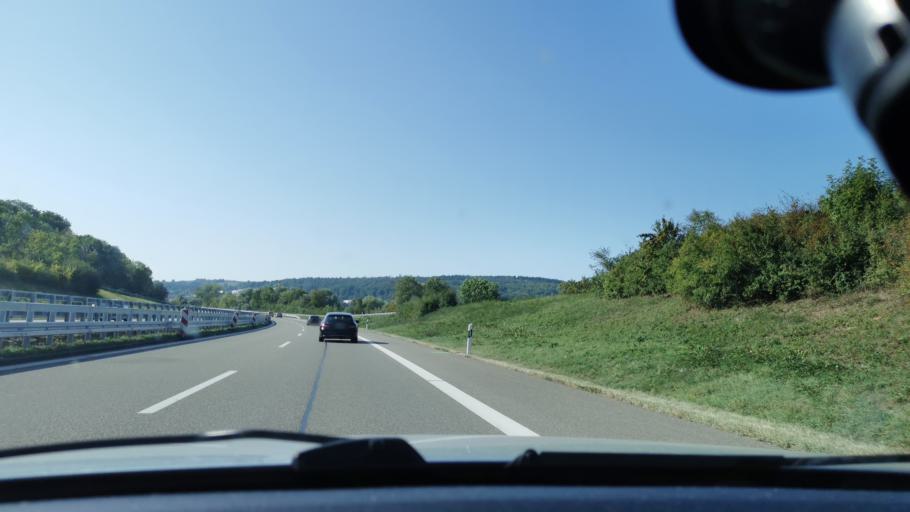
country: DE
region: Baden-Wuerttemberg
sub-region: Regierungsbezirk Stuttgart
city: Albershausen
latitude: 48.7147
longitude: 9.5567
